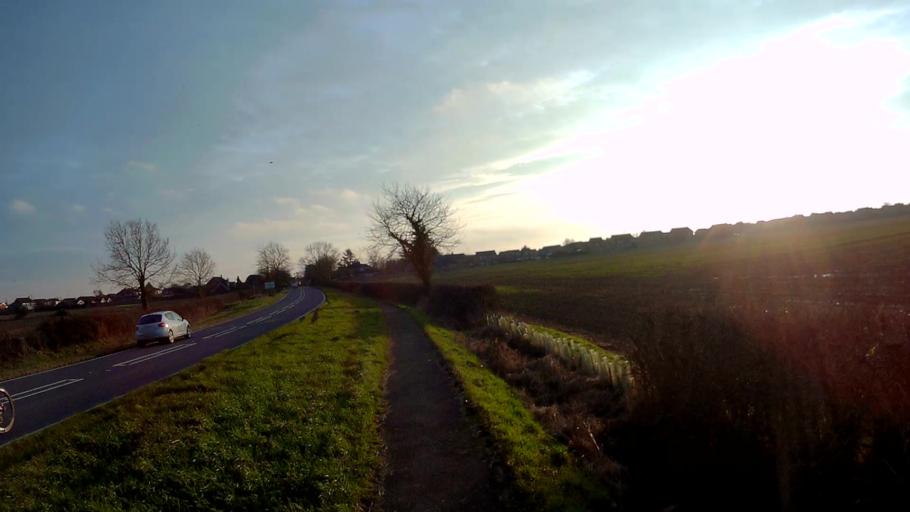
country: GB
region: England
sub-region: Lincolnshire
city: Bourne
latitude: 52.7812
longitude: -0.3770
